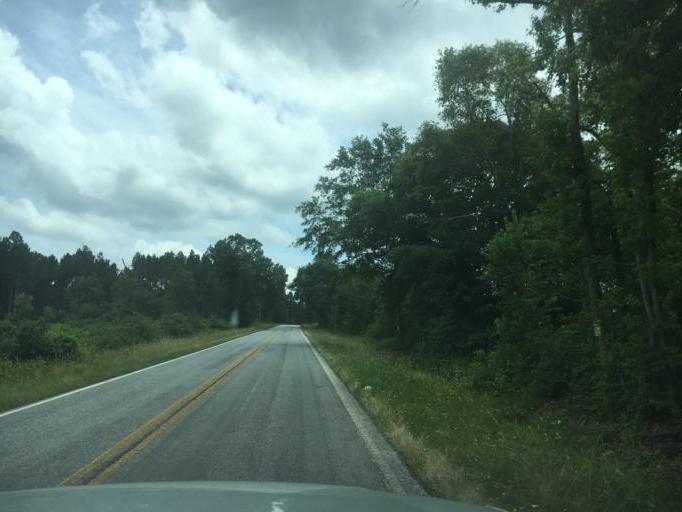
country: US
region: Georgia
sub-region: Hart County
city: Reed Creek
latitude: 34.4309
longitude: -82.9520
